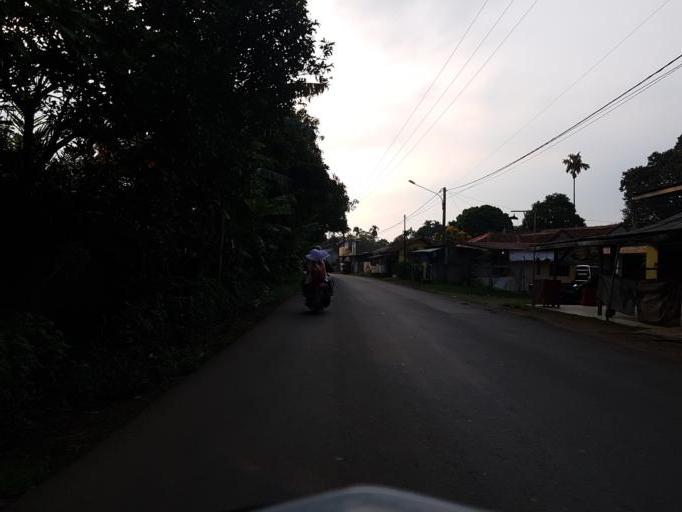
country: ID
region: West Java
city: Parung
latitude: -6.4690
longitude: 106.7157
